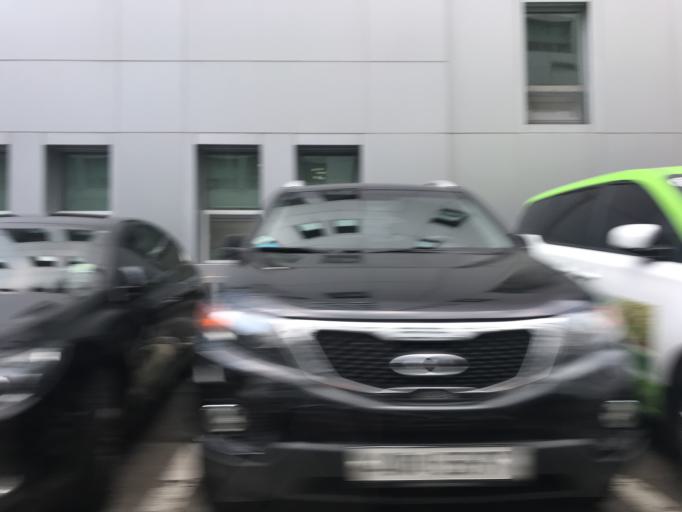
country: KR
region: Seoul
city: Seoul
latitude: 37.5628
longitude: 126.9398
